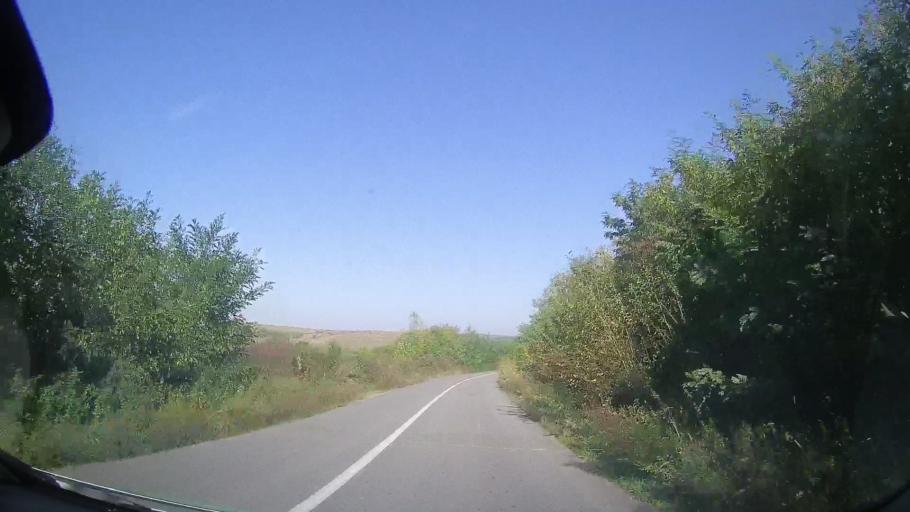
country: RO
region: Timis
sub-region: Comuna Balint
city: Balint
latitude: 45.8354
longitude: 21.8563
